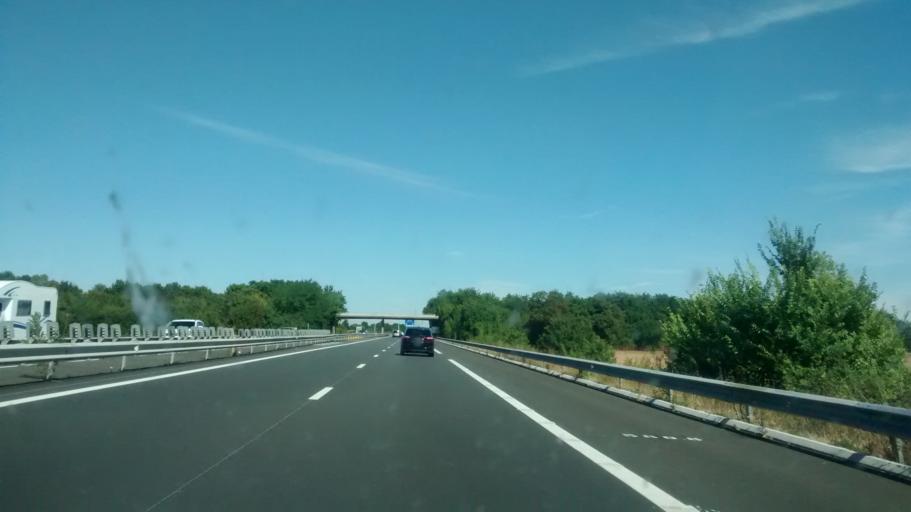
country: FR
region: Poitou-Charentes
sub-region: Departement des Deux-Sevres
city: Fors
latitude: 46.2303
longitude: -0.4424
